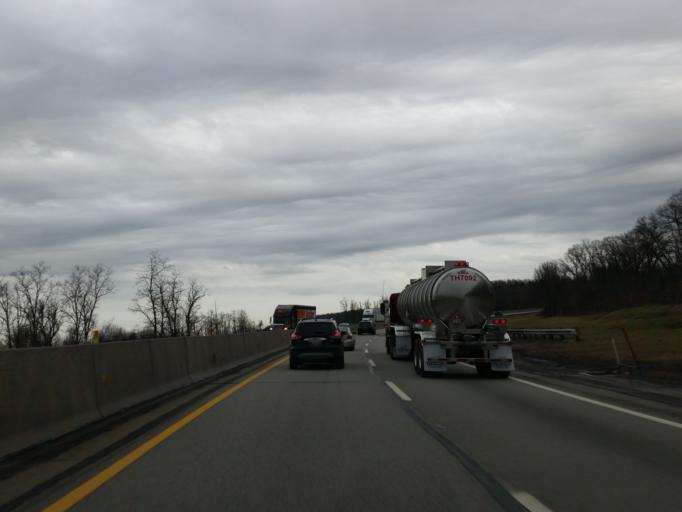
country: US
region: Pennsylvania
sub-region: Somerset County
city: Somerset
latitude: 40.0654
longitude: -79.1444
